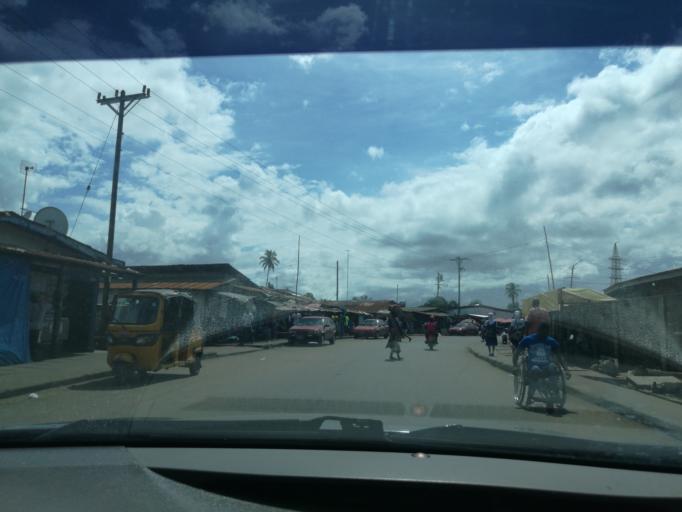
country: LR
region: Montserrado
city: Monrovia
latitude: 6.3280
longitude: -10.7977
